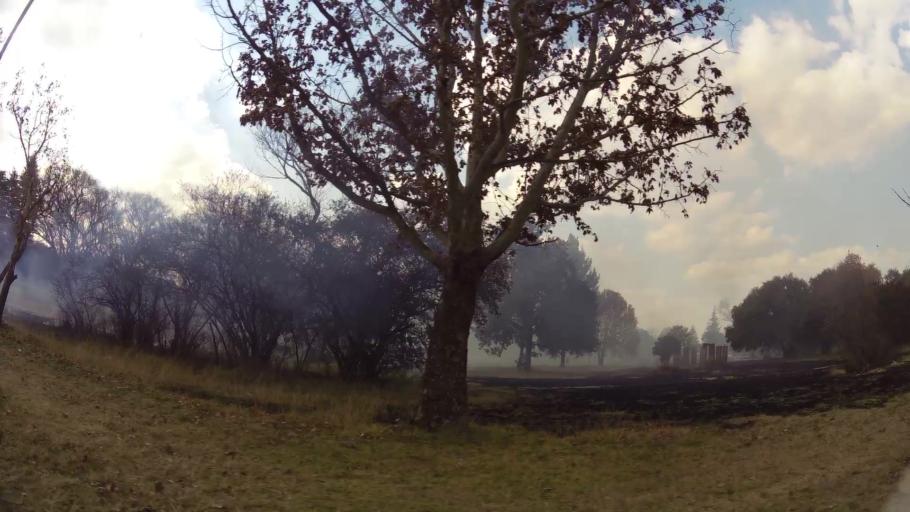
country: ZA
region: Mpumalanga
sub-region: Nkangala District Municipality
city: Delmas
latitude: -26.1445
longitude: 28.6705
